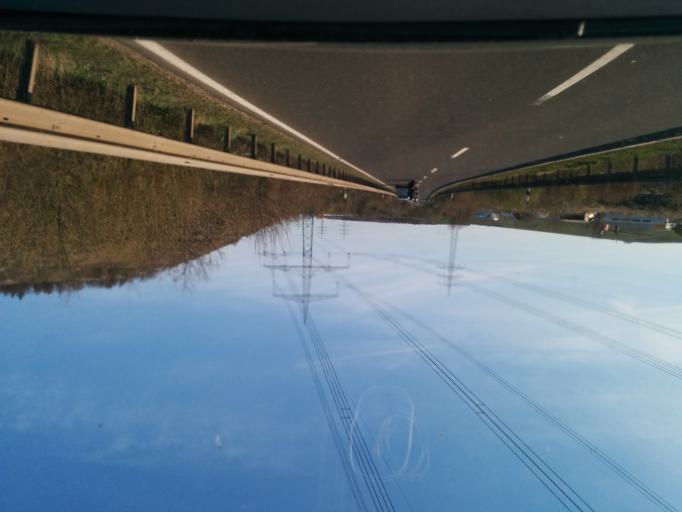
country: DE
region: Rheinland-Pfalz
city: Windesheim
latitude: 49.9082
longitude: 7.8231
